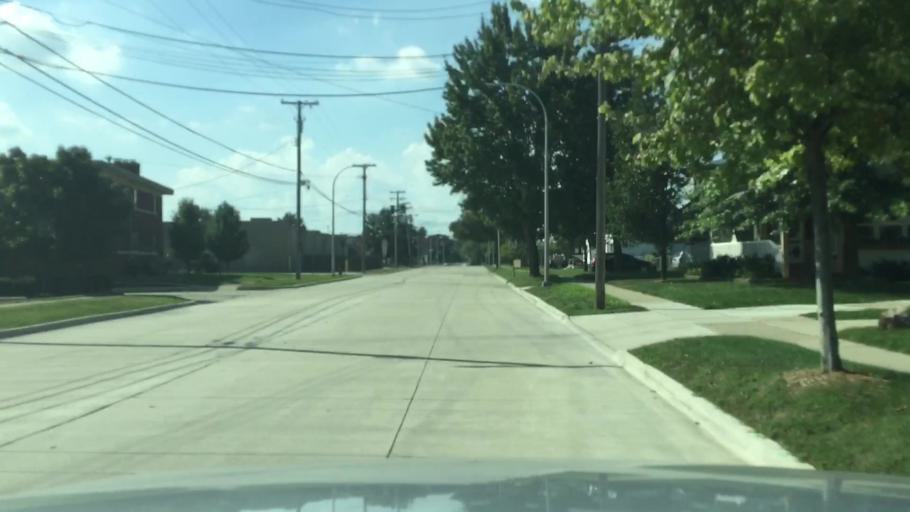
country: US
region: Michigan
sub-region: Wayne County
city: Wayne
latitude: 42.2825
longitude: -83.3787
